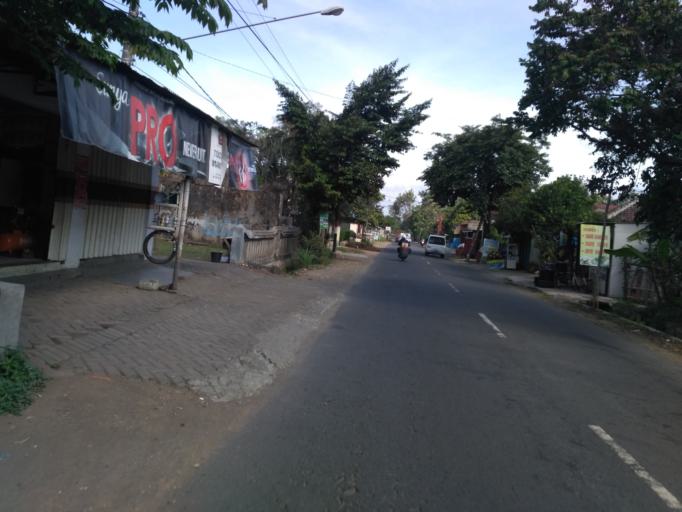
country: ID
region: East Java
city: Golek
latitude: -8.0688
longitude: 112.6265
